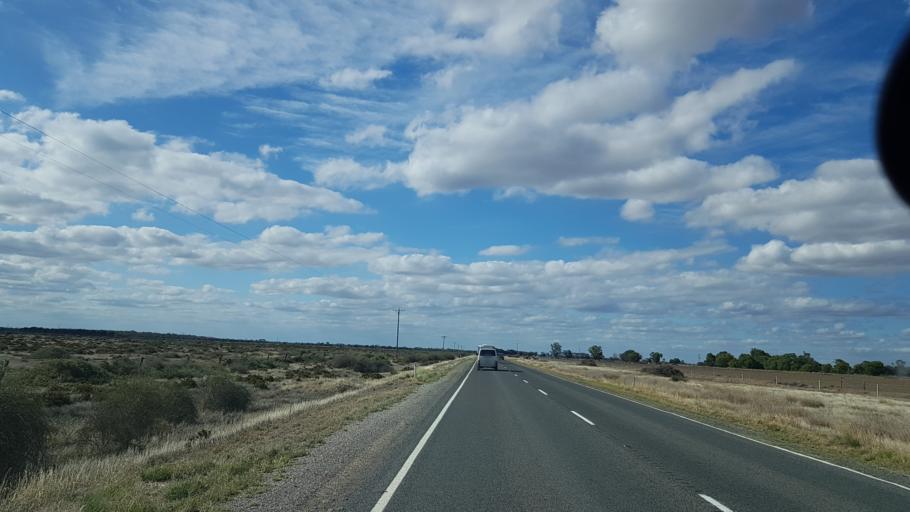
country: AU
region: Victoria
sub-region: Swan Hill
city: Swan Hill
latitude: -35.8401
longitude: 143.9399
